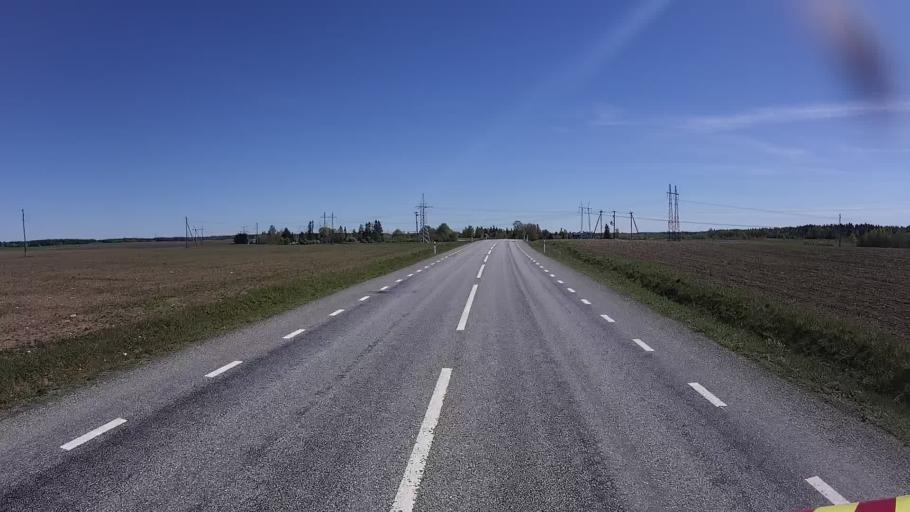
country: EE
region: Laeaene-Virumaa
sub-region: Tapa vald
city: Tapa
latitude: 59.2378
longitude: 25.7019
